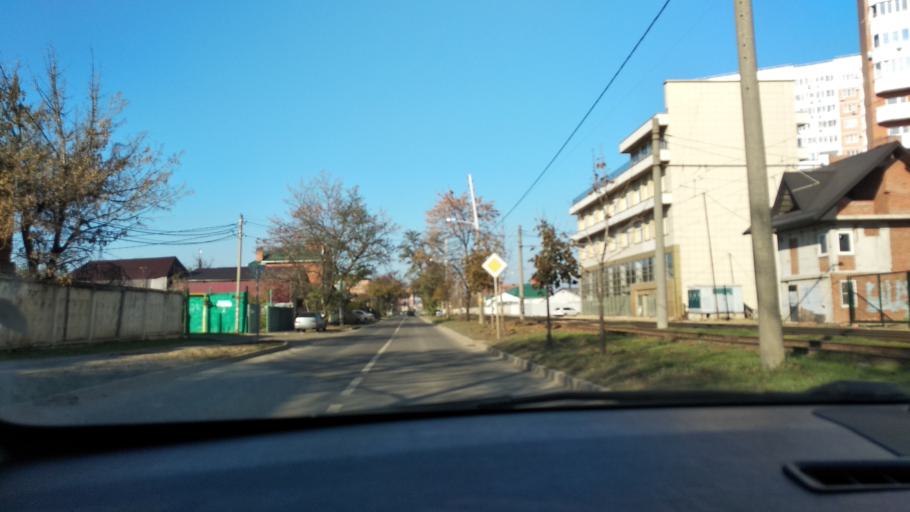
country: RU
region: Krasnodarskiy
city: Krasnodar
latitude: 45.0035
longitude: 39.0202
